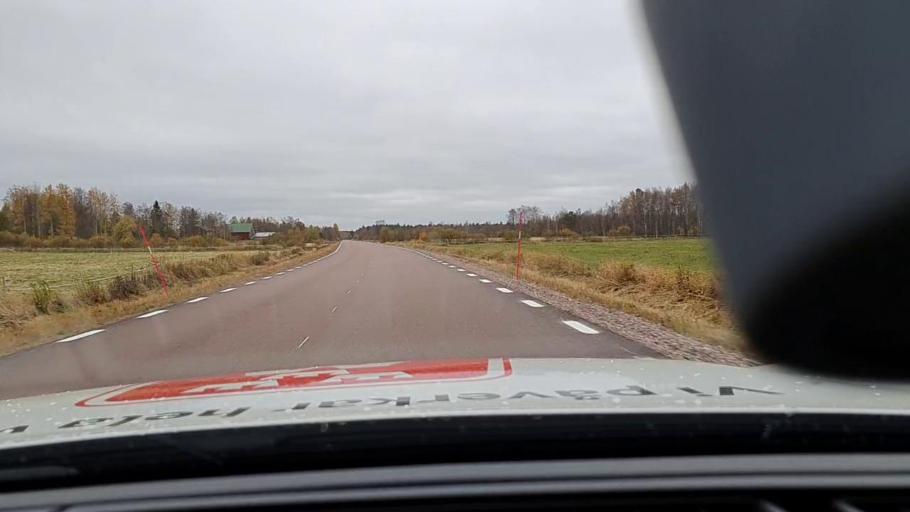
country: FI
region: Lapland
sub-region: Kemi-Tornio
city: Tornio
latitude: 66.0605
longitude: 23.9269
